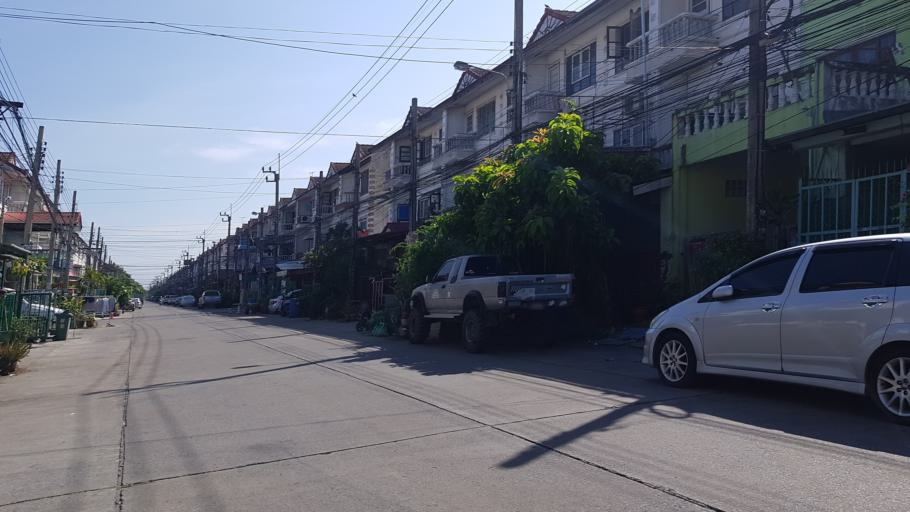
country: TH
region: Bangkok
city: Khlong Sam Wa
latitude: 13.8503
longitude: 100.7226
